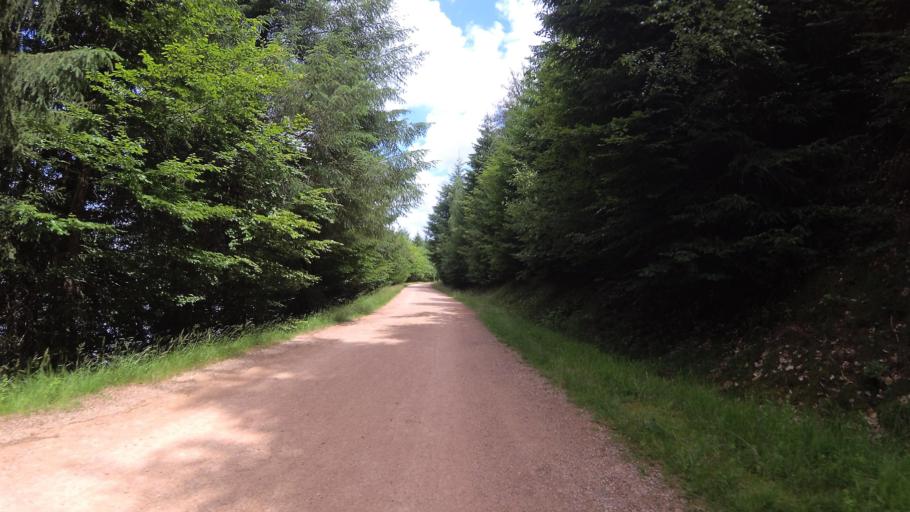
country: DE
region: Rheinland-Pfalz
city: Neuhutten
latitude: 49.6172
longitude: 6.9870
